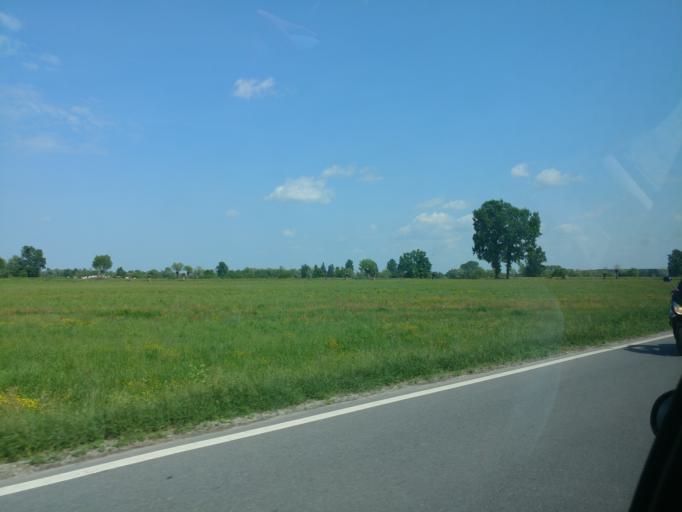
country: IT
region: Piedmont
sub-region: Provincia di Cuneo
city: Carde
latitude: 44.7242
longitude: 7.4358
